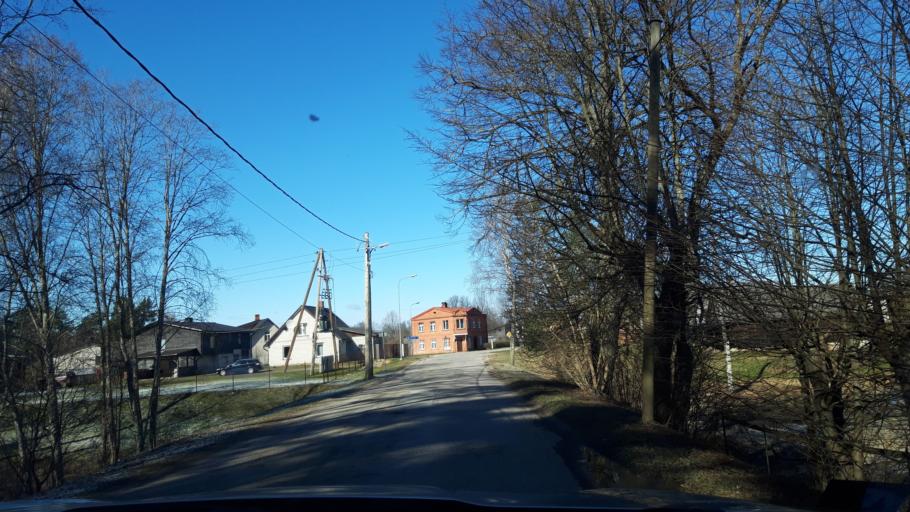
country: LV
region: Strenci
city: Strenci
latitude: 57.6232
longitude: 25.6952
